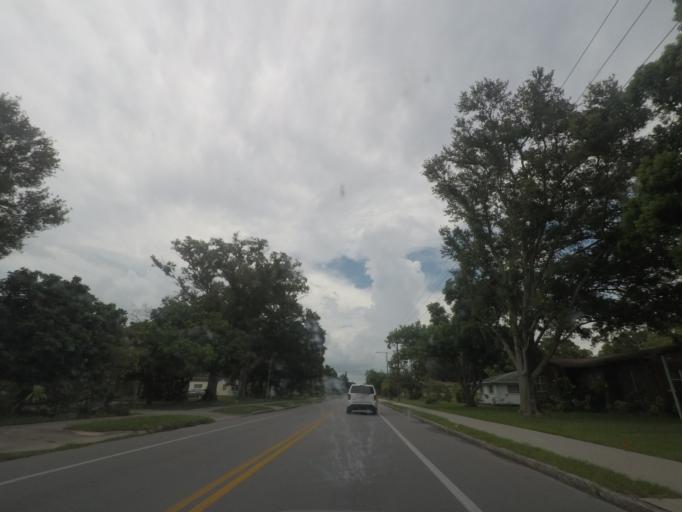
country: US
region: Florida
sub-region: Pinellas County
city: Lealman
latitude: 27.7992
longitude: -82.6751
